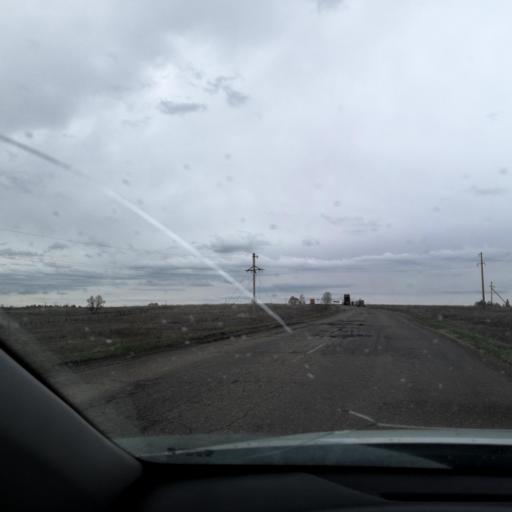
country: RU
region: Bashkortostan
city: Pavlovka
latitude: 55.3191
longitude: 56.3456
